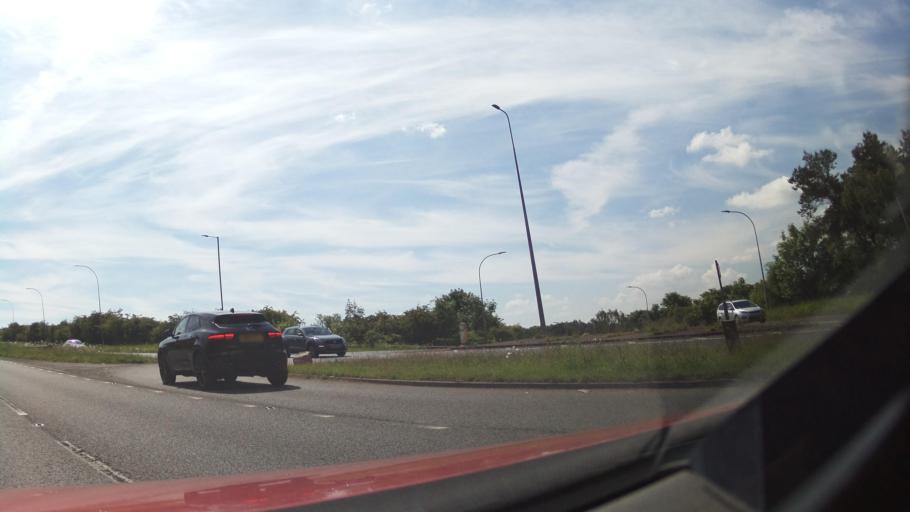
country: GB
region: England
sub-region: North Lincolnshire
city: Broughton
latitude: 53.5555
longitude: -0.5851
